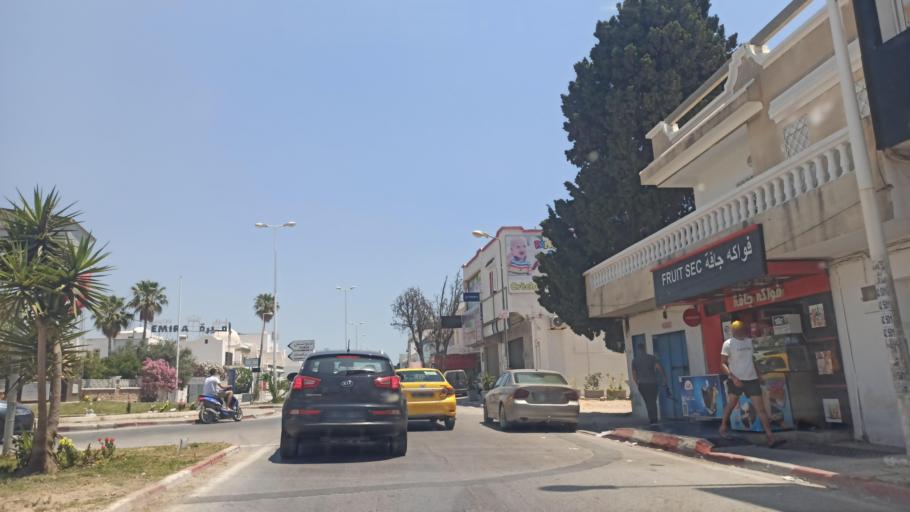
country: TN
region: Nabul
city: Al Hammamat
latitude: 36.4049
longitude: 10.6301
